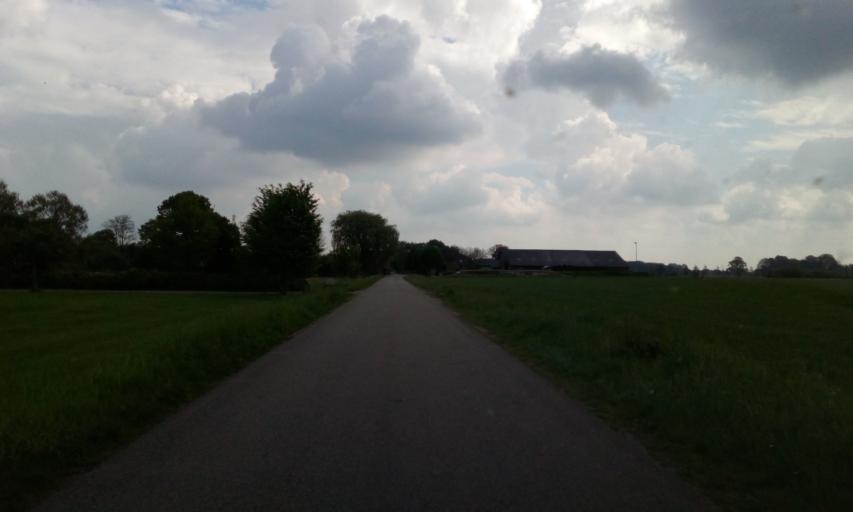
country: NL
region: Gelderland
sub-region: Gemeente Voorst
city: Voorst
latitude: 52.1657
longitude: 6.0881
